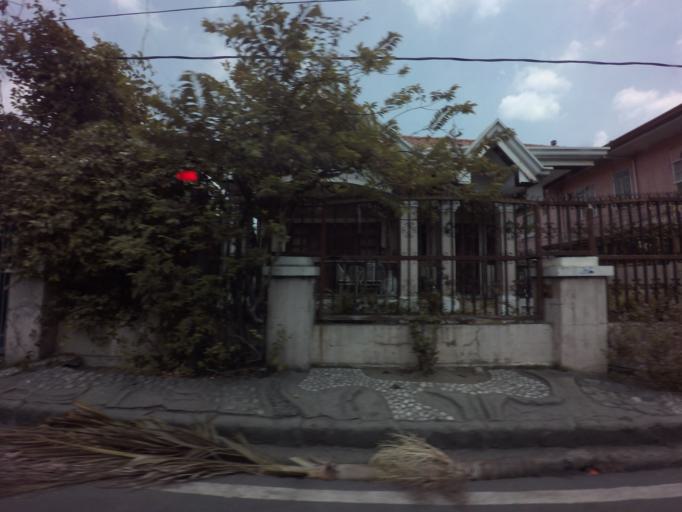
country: PH
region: Calabarzon
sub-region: Province of Rizal
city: Taguig
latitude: 14.4733
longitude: 121.0588
